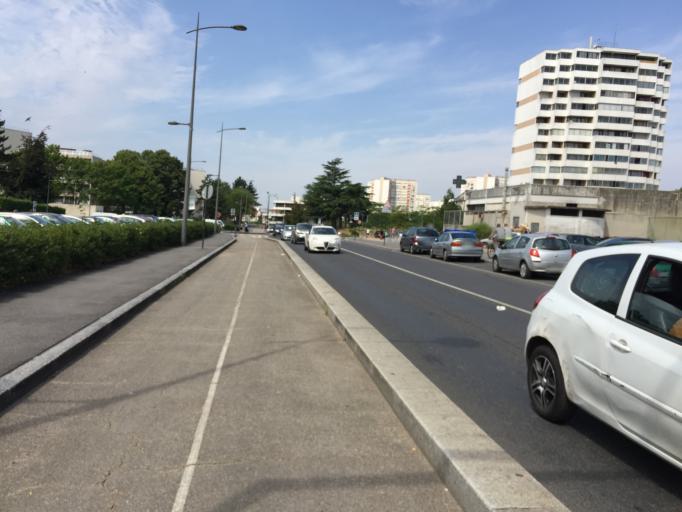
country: FR
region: Ile-de-France
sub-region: Departement de Seine-et-Marne
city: Fublaines
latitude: 48.9511
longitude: 2.9137
